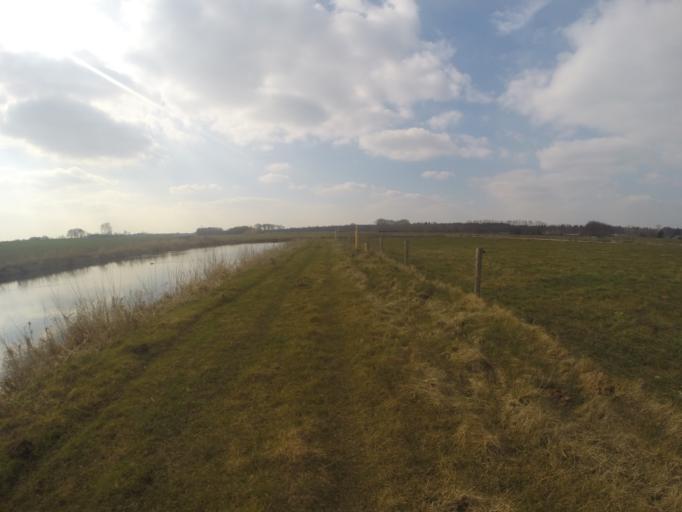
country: NL
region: Gelderland
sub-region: Gemeente Lochem
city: Almen
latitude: 52.1526
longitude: 6.2872
